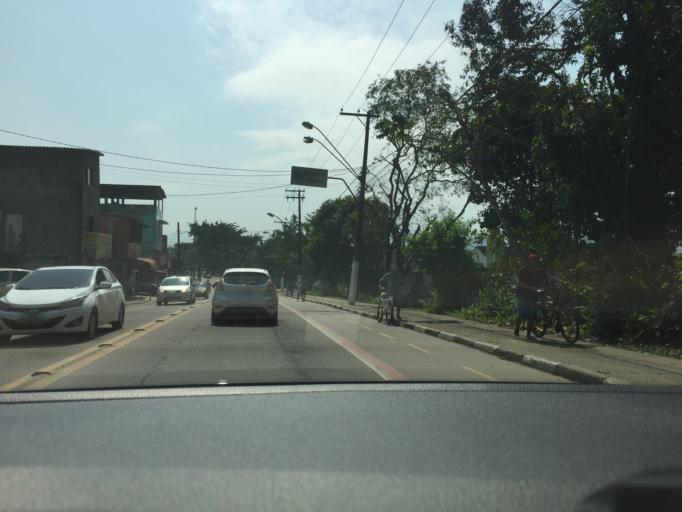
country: BR
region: Sao Paulo
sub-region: Guaruja
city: Guaruja
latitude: -23.9774
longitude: -46.2508
